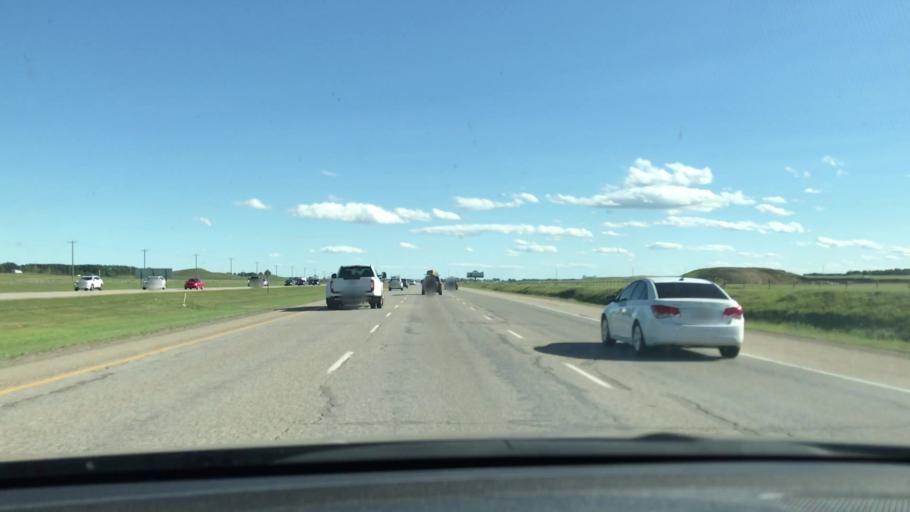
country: CA
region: Alberta
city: Airdrie
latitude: 51.2550
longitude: -114.0020
